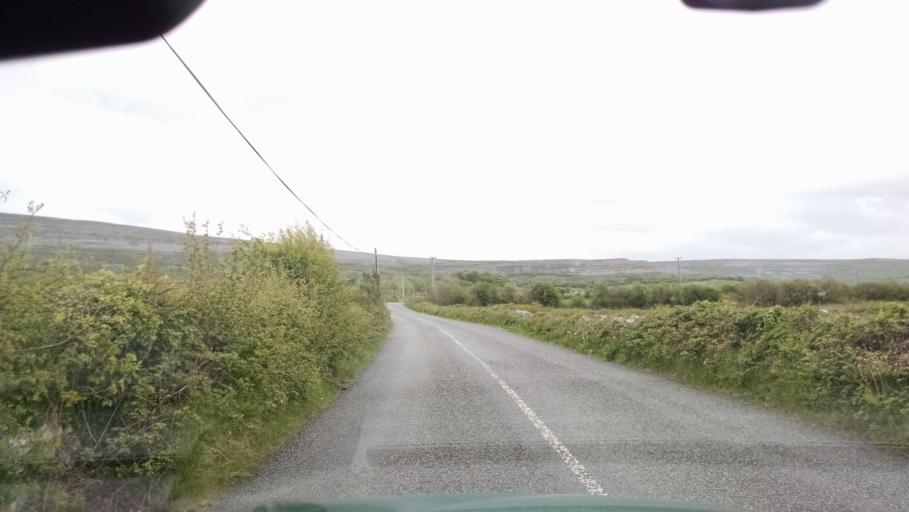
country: IE
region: Connaught
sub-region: County Galway
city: Bearna
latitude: 53.0969
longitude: -9.1594
